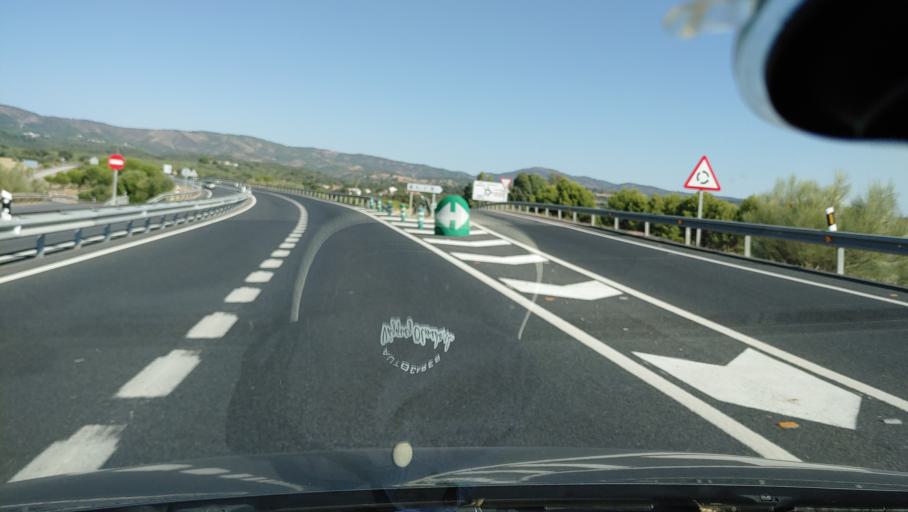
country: ES
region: Andalusia
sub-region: Province of Cordoba
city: Cordoba
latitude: 37.9176
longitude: -4.7602
